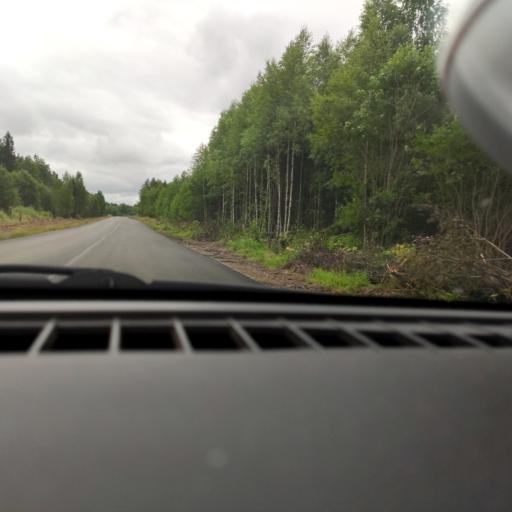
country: RU
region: Perm
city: Polazna
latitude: 58.3351
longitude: 56.1926
